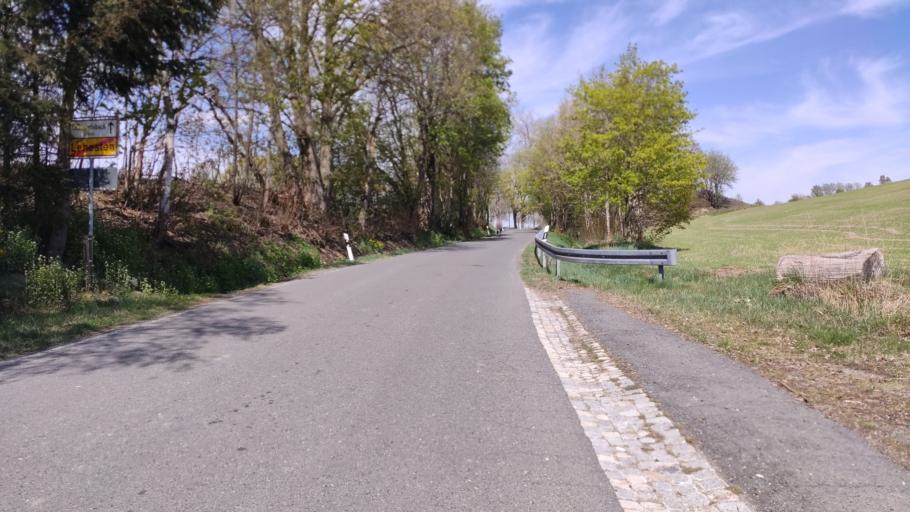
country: DE
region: Bavaria
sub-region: Upper Franconia
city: Ludwigsstadt
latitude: 50.4796
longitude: 11.4423
